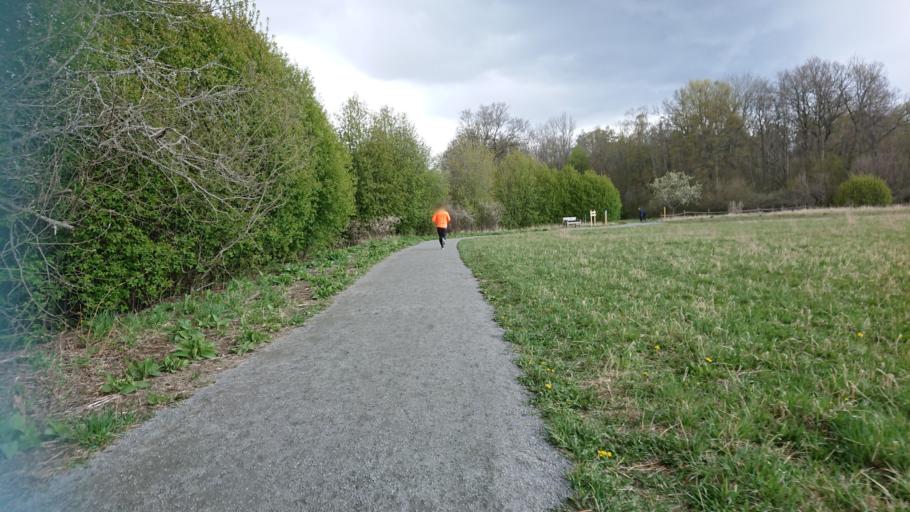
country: SE
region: Uppsala
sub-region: Uppsala Kommun
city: Uppsala
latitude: 59.7985
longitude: 17.6077
